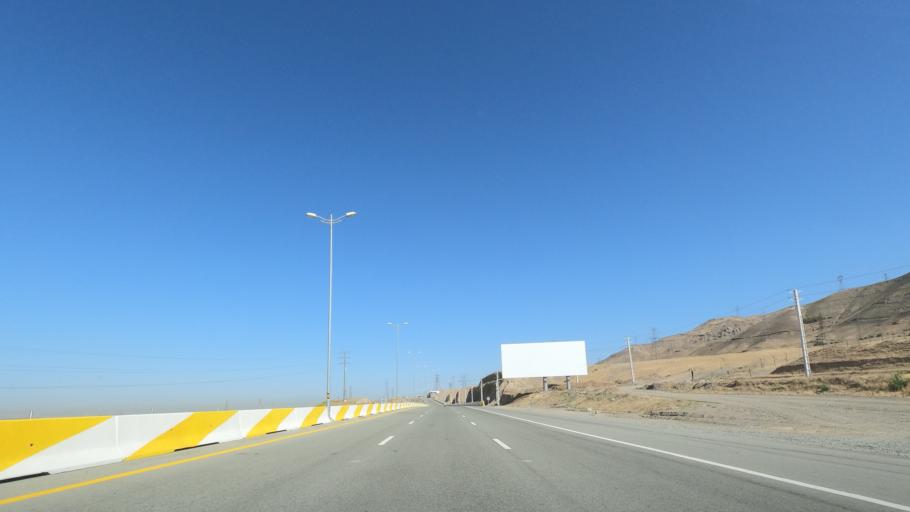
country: IR
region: Tehran
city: Shahr-e Qods
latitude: 35.7701
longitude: 51.0611
